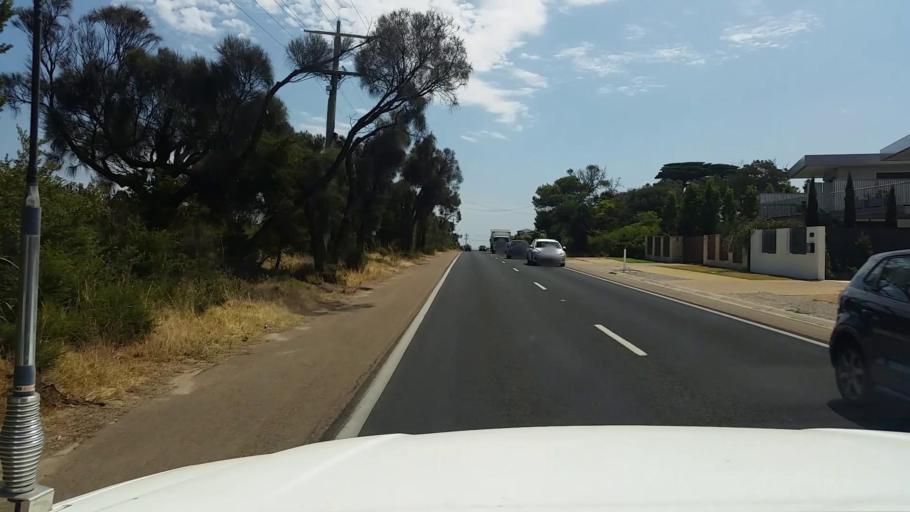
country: AU
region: Victoria
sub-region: Mornington Peninsula
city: Mornington
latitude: -38.2329
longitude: 145.0273
